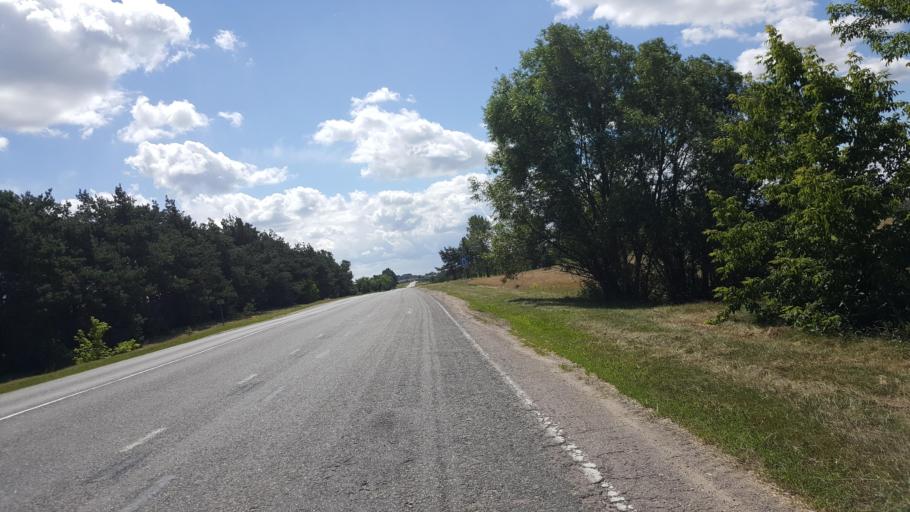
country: BY
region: Brest
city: Kamyanyets
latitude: 52.3384
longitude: 23.9090
